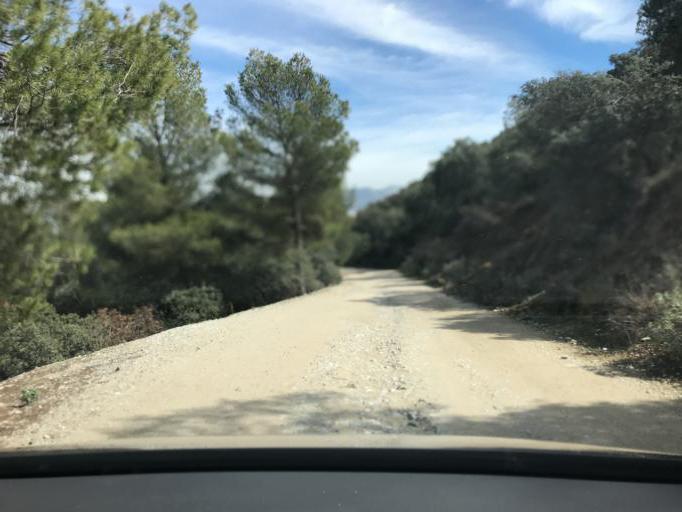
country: ES
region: Andalusia
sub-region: Provincia de Granada
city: Atarfe
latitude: 37.2474
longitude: -3.6839
